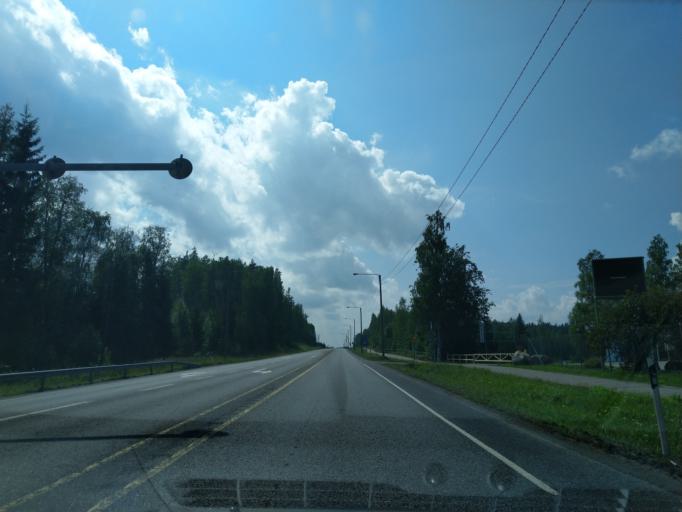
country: FI
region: South Karelia
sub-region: Imatra
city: Ruokolahti
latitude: 61.2657
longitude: 28.9215
